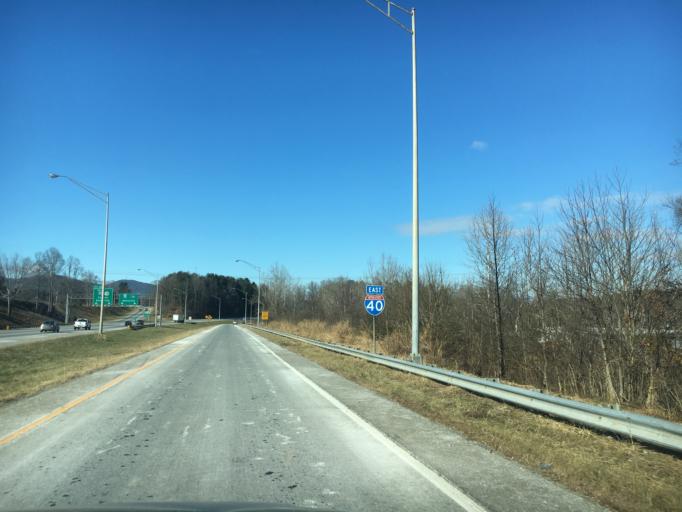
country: US
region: North Carolina
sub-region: Buncombe County
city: Bent Creek
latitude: 35.5491
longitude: -82.6070
